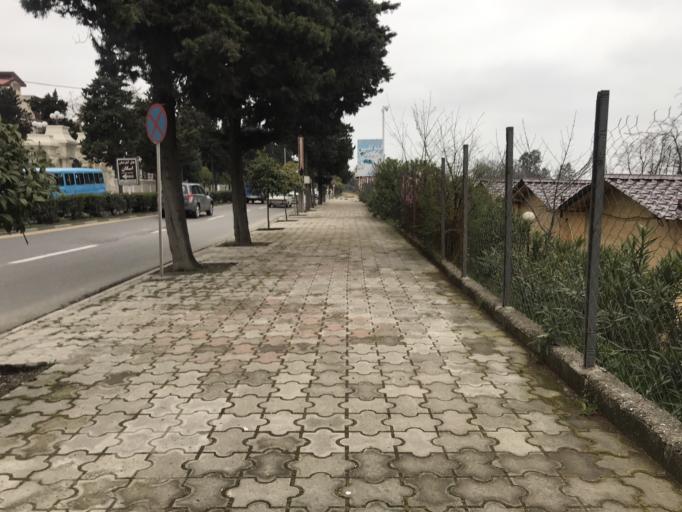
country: IR
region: Mazandaran
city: Ramsar
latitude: 36.9230
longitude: 50.6706
